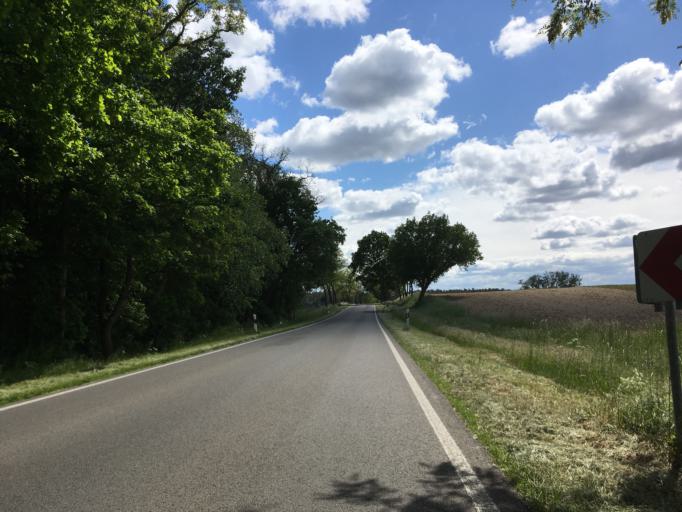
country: DE
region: Brandenburg
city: Protzel
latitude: 52.6703
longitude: 13.9915
